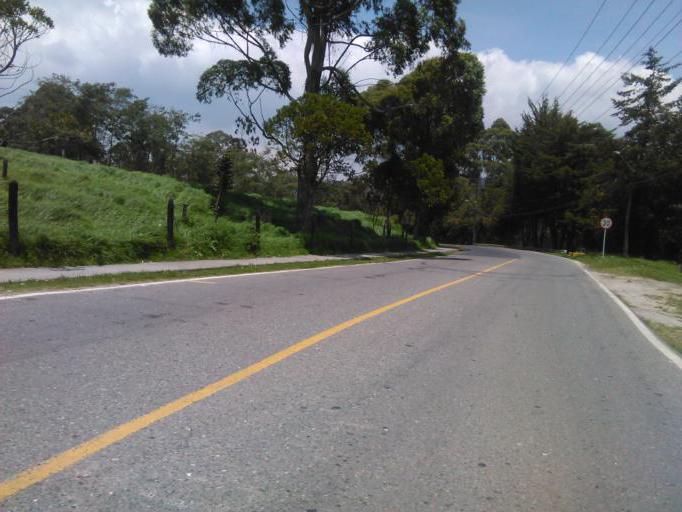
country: CO
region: Antioquia
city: La Union
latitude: 5.9790
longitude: -75.3681
